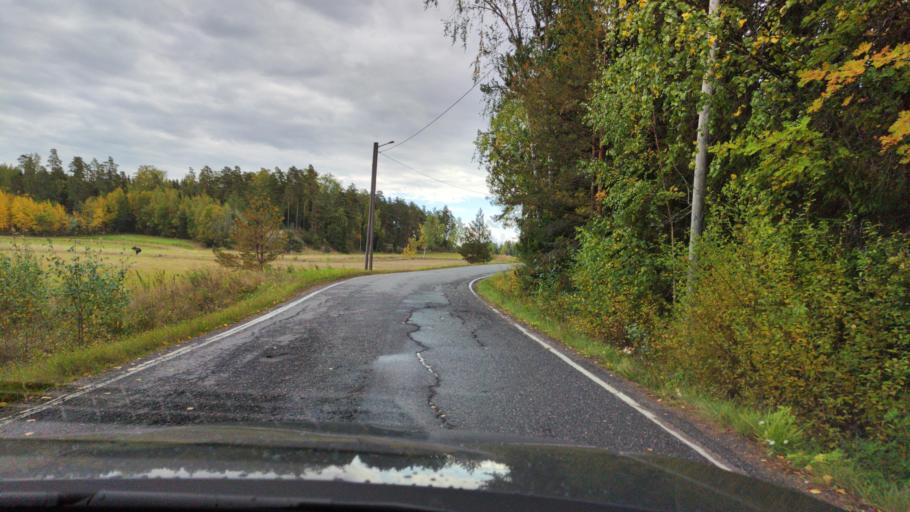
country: FI
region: Varsinais-Suomi
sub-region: Aboland-Turunmaa
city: Pargas
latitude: 60.3681
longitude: 22.2759
